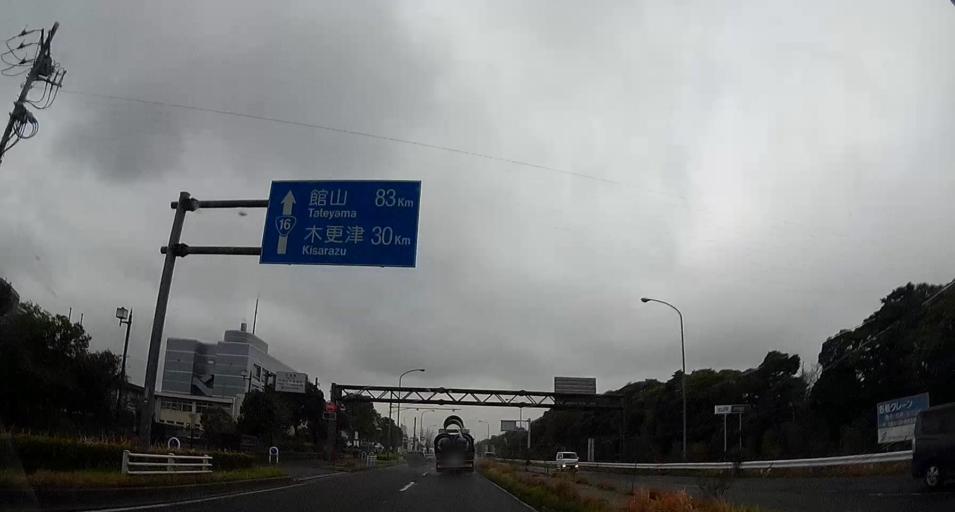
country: JP
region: Chiba
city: Ichihara
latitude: 35.5356
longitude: 140.1096
